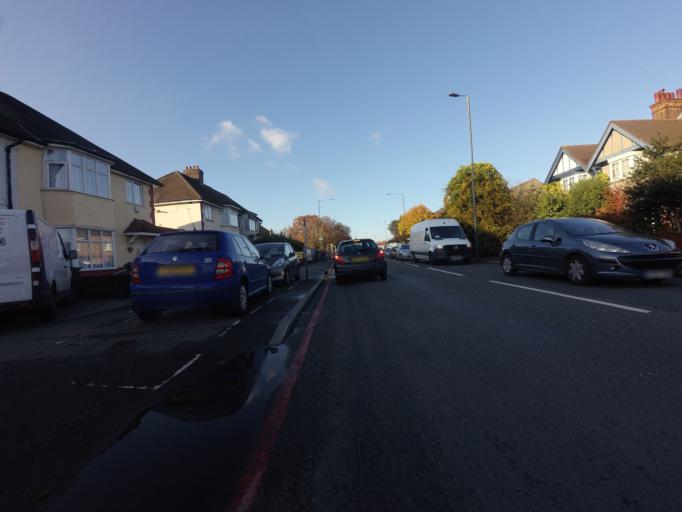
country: GB
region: England
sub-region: Greater London
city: Feltham
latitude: 51.4512
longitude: -0.4050
